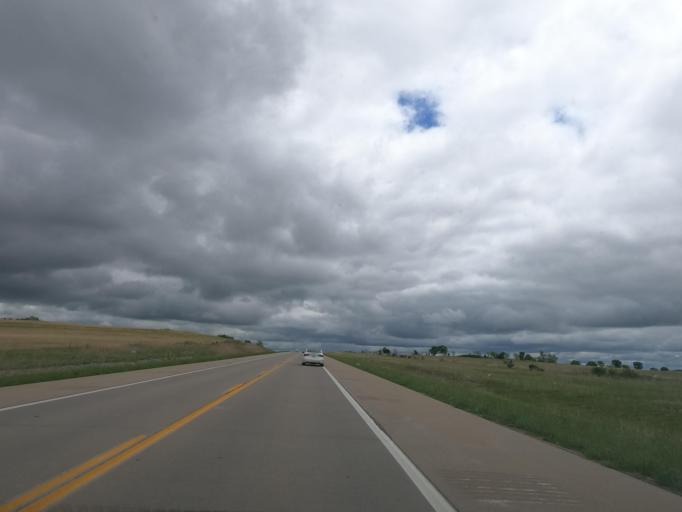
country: US
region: Kansas
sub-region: Montgomery County
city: Cherryvale
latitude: 37.3472
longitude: -95.5716
